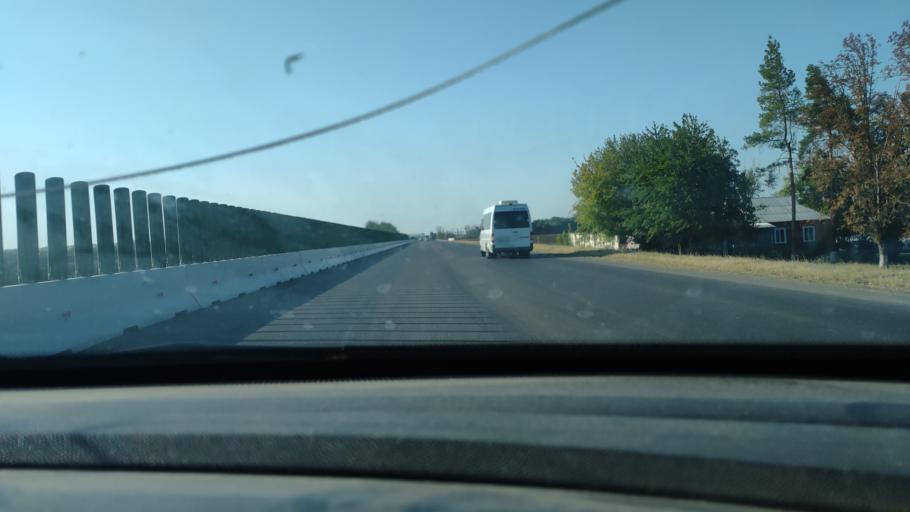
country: RU
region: Krasnodarskiy
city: Medvedovskaya
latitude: 45.4767
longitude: 38.9716
